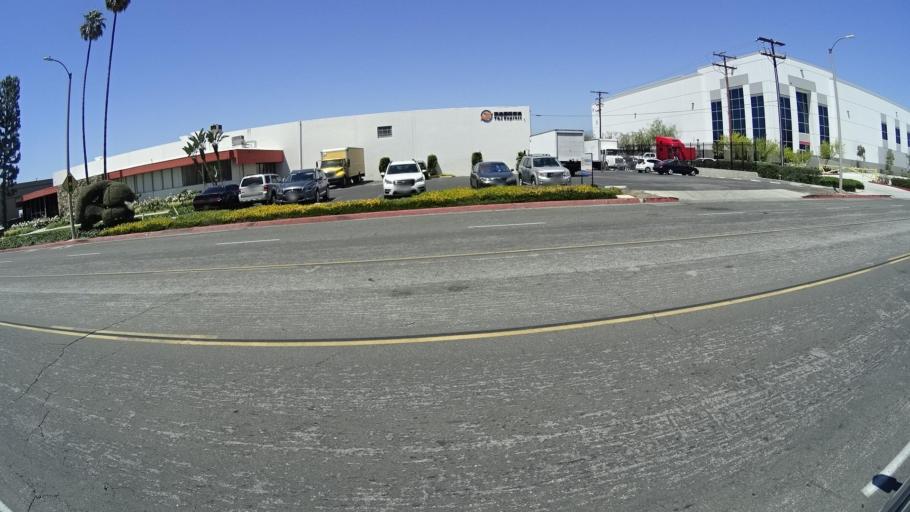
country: US
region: California
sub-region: Los Angeles County
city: La Puente
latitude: 34.0231
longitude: -117.9684
